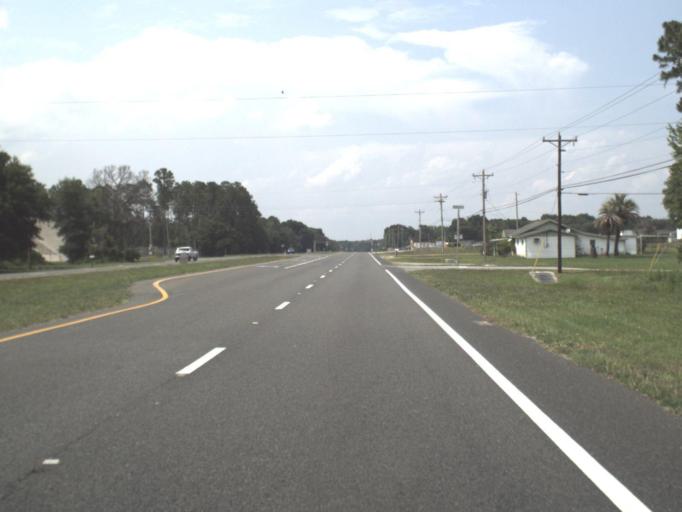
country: US
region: Florida
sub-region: Clay County
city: Green Cove Springs
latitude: 29.8664
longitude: -81.6634
